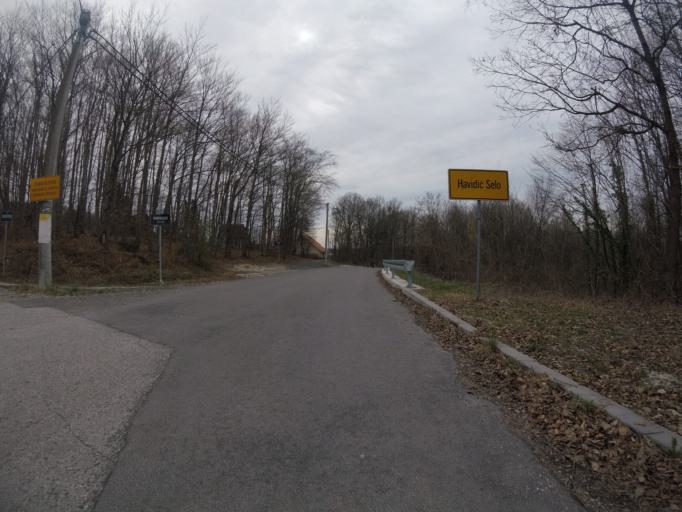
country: HR
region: Grad Zagreb
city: Strmec
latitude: 45.6341
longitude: 15.9358
